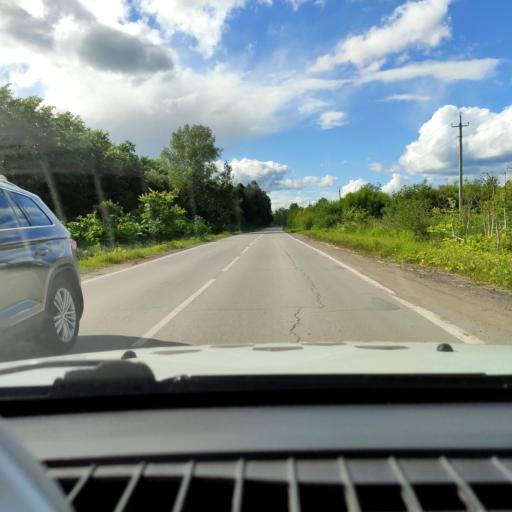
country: RU
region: Perm
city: Overyata
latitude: 58.0999
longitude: 55.8550
